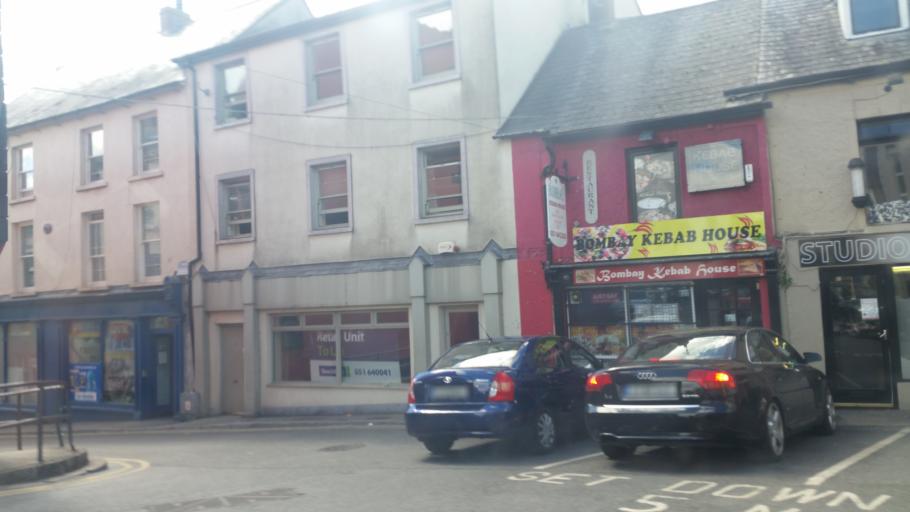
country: IE
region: Munster
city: Carrick-on-Suir
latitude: 52.3465
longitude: -7.4143
